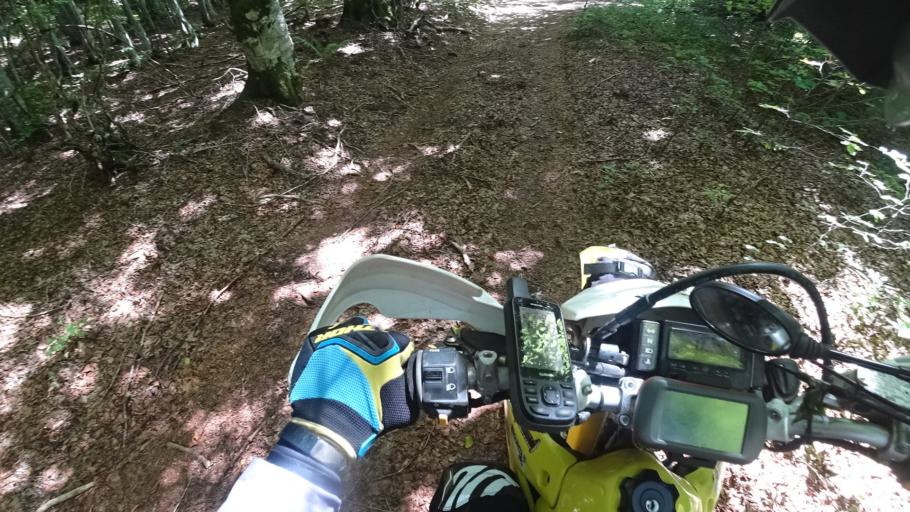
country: HR
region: Zadarska
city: Gracac
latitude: 44.4274
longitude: 15.9991
